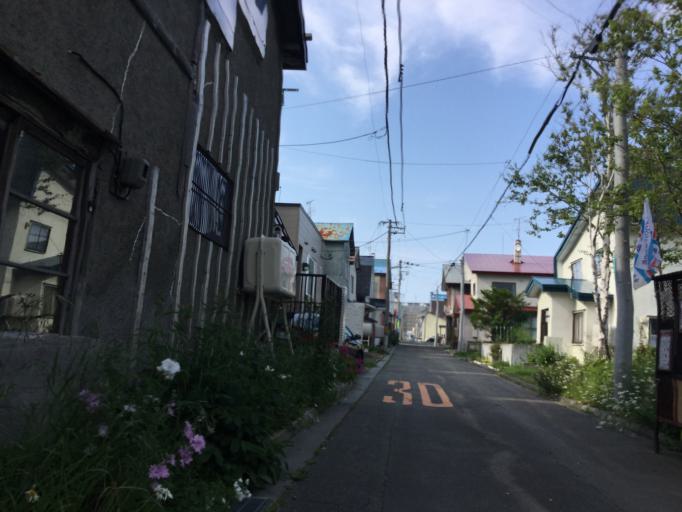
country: JP
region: Hokkaido
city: Wakkanai
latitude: 45.4131
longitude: 141.6745
